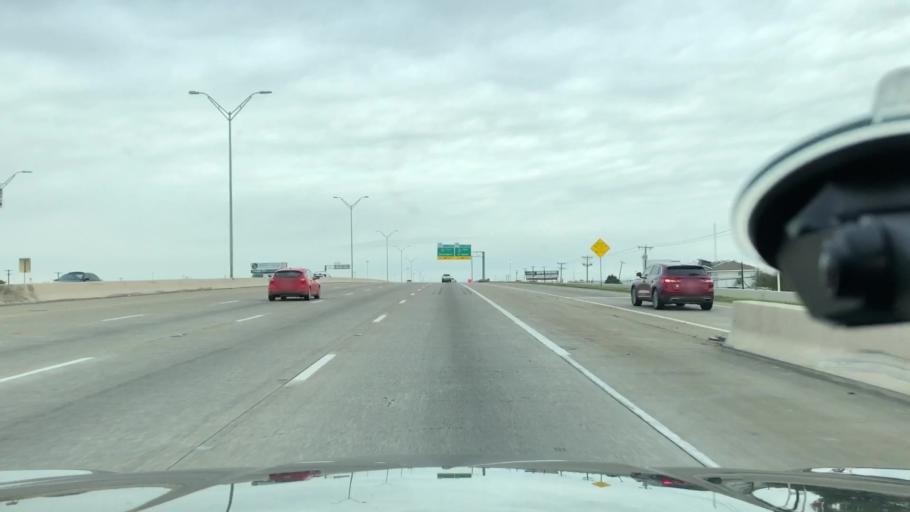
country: US
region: Texas
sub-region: Dallas County
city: DeSoto
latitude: 32.6308
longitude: -96.8230
